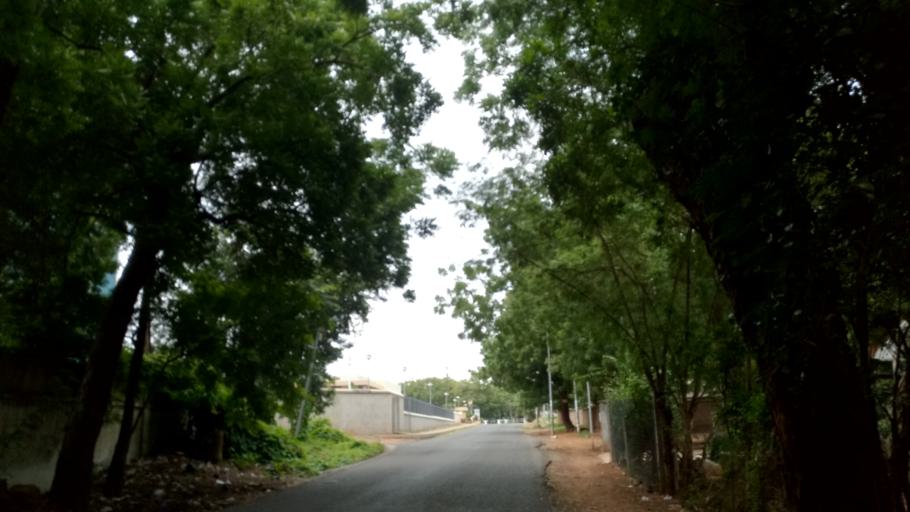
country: GH
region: Greater Accra
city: Accra
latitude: 5.5584
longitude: -0.1925
